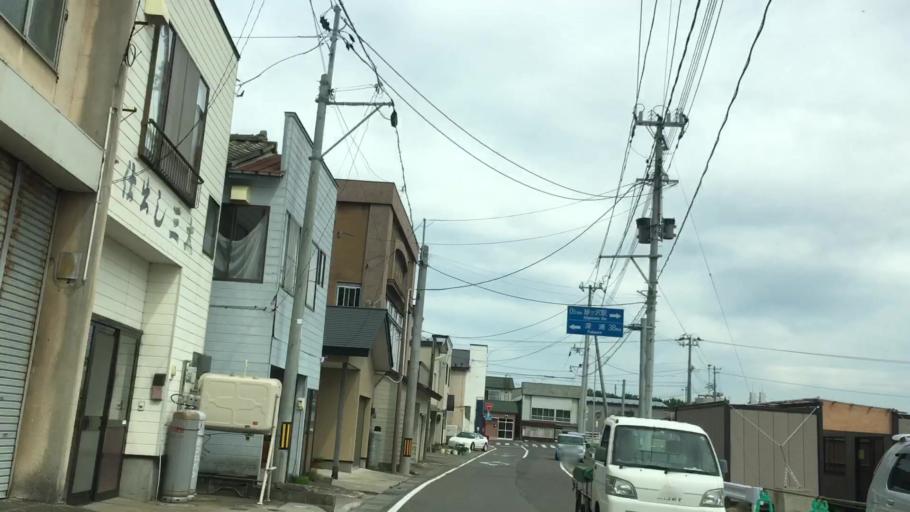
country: JP
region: Aomori
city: Shimokizukuri
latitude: 40.7771
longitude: 140.2173
